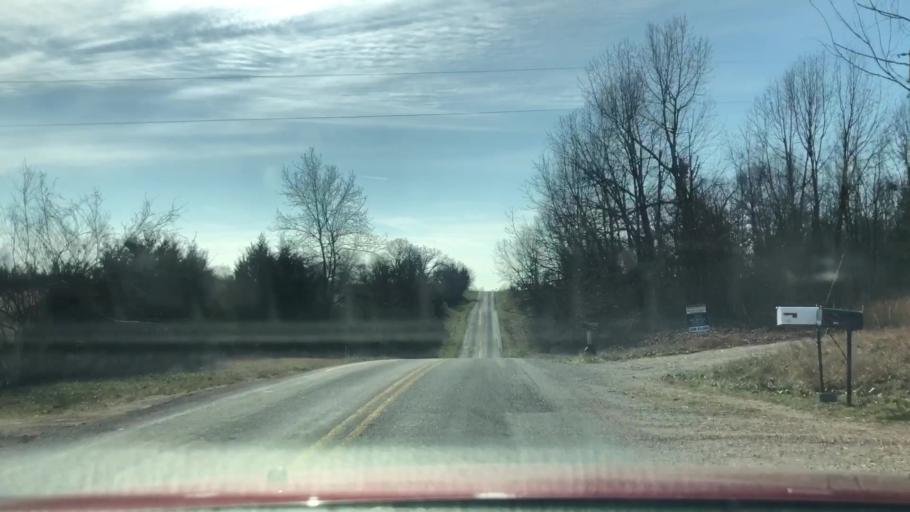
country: US
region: Missouri
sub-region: Wright County
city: Mansfield
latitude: 37.1089
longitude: -92.6295
